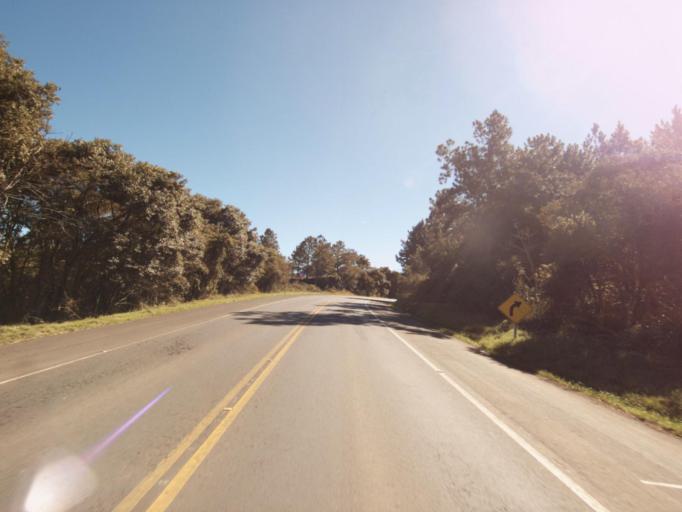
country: BR
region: Santa Catarina
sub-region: Joacaba
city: Joacaba
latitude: -27.1149
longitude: -51.6315
